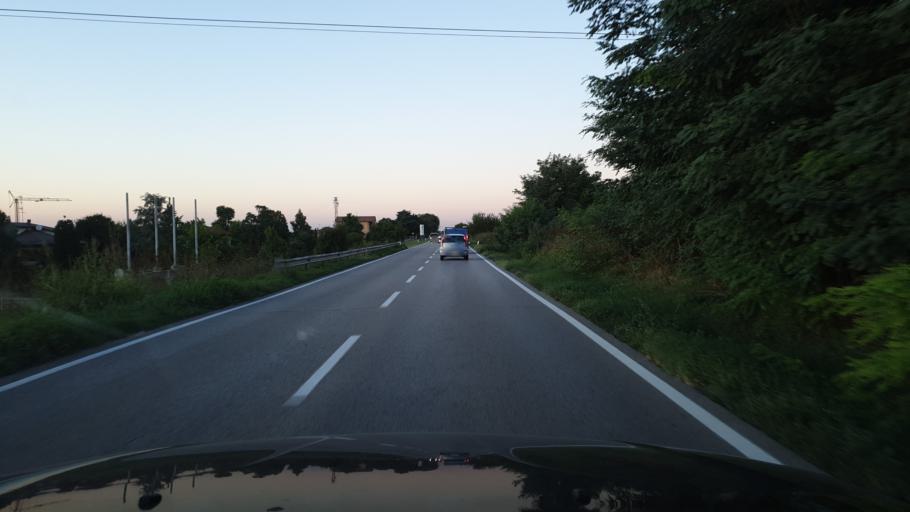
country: IT
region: Emilia-Romagna
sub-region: Provincia di Bologna
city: Ca De Fabbri
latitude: 44.6049
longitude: 11.4427
